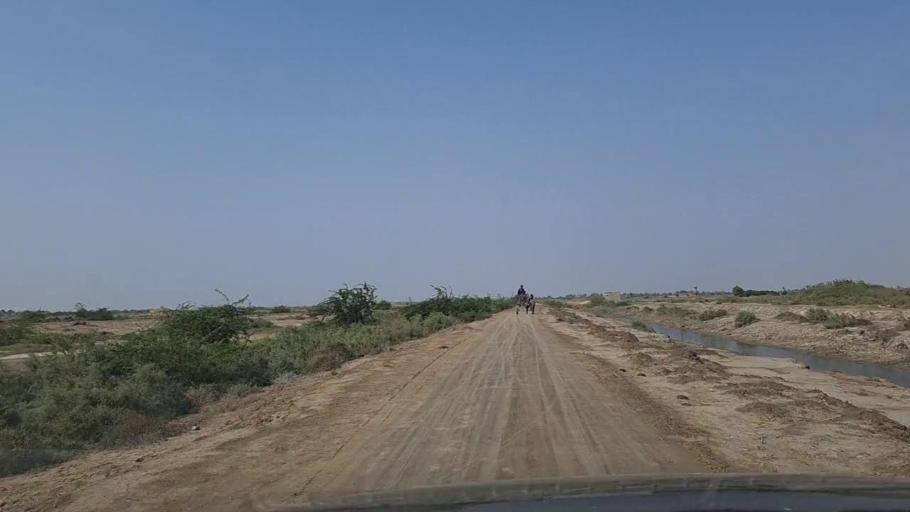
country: PK
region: Sindh
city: Gharo
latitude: 24.7032
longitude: 67.5837
